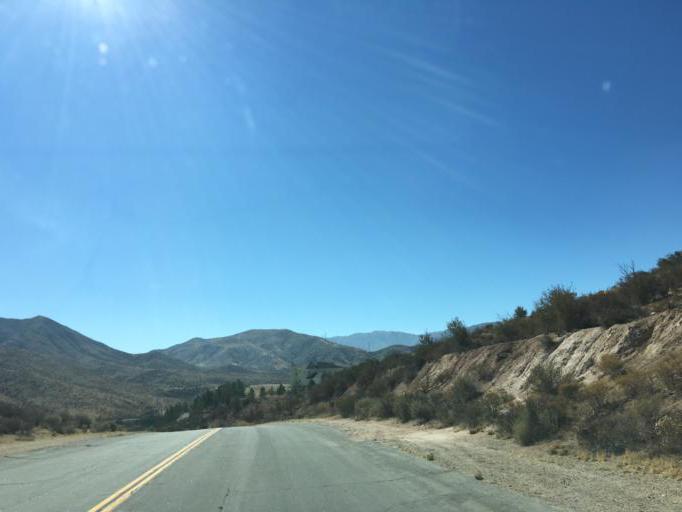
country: US
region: California
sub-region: Los Angeles County
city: Acton
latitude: 34.4599
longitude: -118.1624
